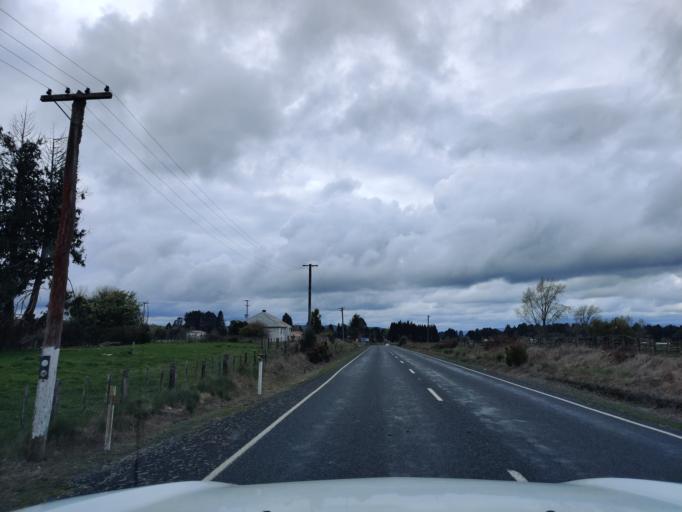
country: NZ
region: Waikato
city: Turangi
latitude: -39.0064
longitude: 175.3770
